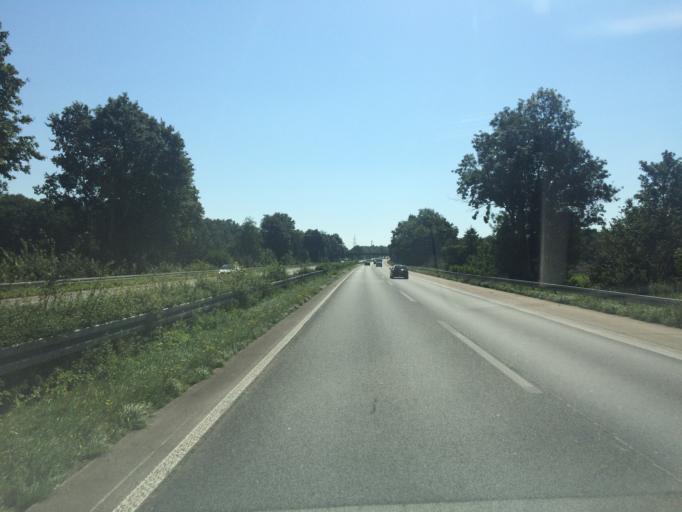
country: DE
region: North Rhine-Westphalia
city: Werne
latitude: 51.6882
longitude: 7.6729
